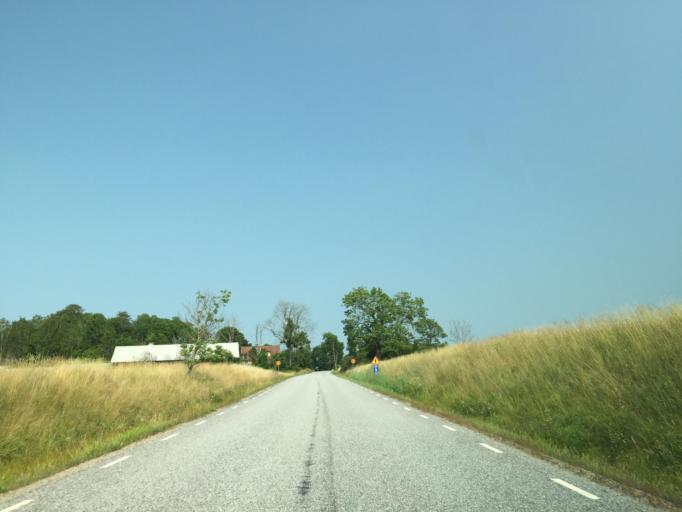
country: SE
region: Vaestra Goetaland
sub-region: Lilla Edets Kommun
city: Lilla Edet
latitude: 58.2095
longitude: 12.1334
